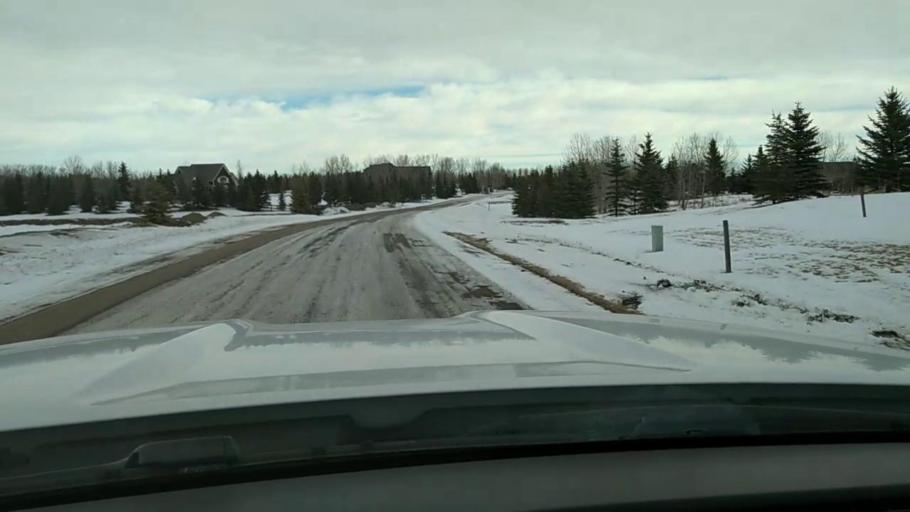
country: CA
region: Alberta
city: Cochrane
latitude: 51.2070
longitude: -114.2895
